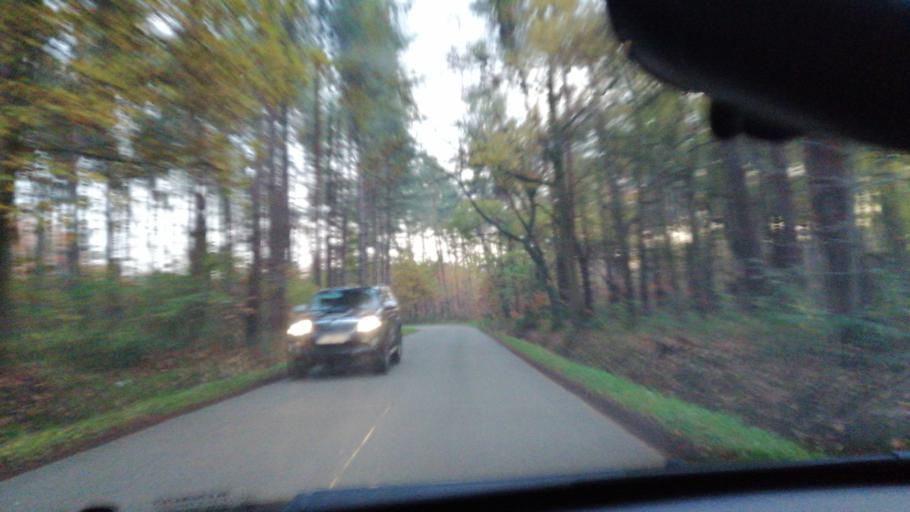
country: BE
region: Flanders
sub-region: Provincie Antwerpen
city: Lille
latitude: 51.2200
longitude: 4.8259
